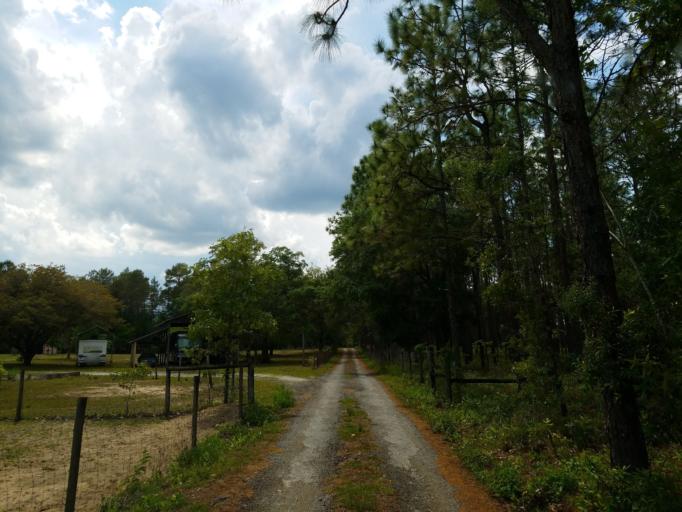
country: US
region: Florida
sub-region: Hernando County
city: Hill 'n Dale
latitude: 28.5301
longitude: -82.2570
